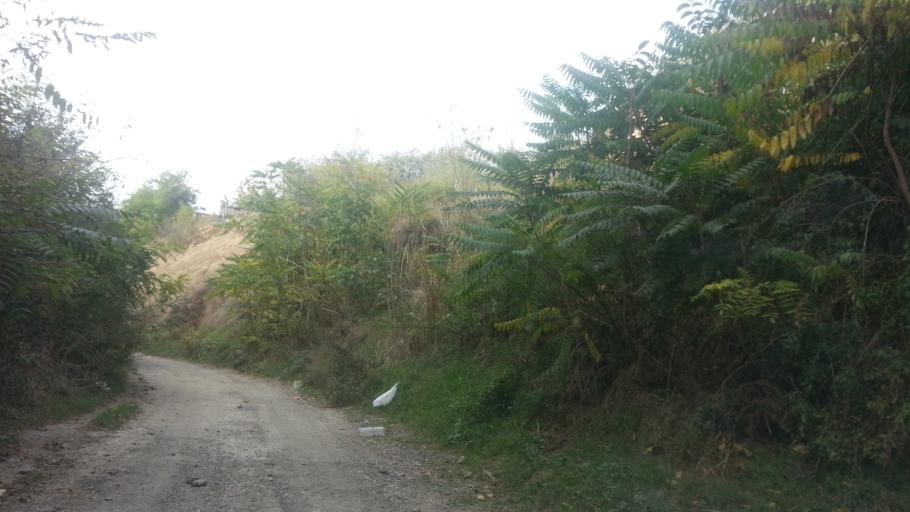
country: RS
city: Belegis
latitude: 45.0218
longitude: 20.3462
